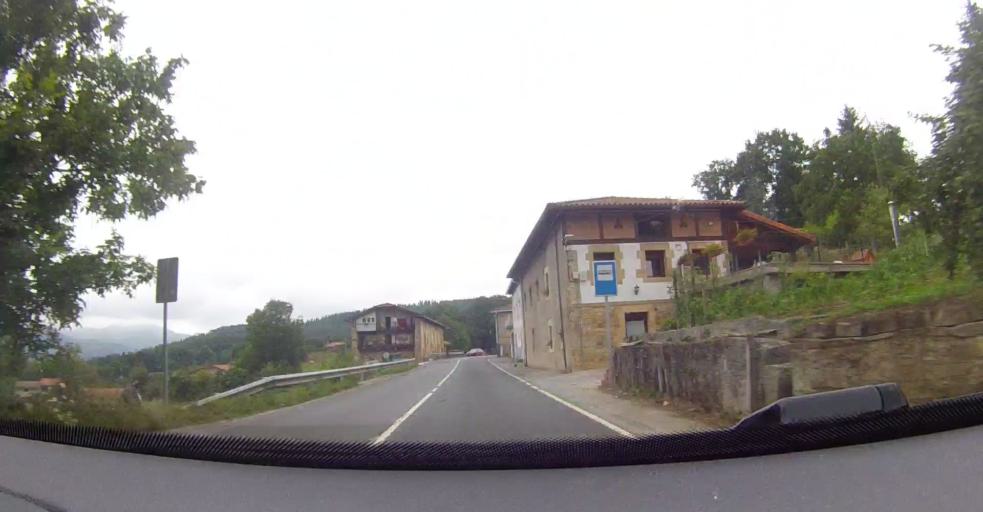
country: ES
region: Basque Country
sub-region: Bizkaia
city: Balmaseda
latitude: 43.2425
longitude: -3.2384
